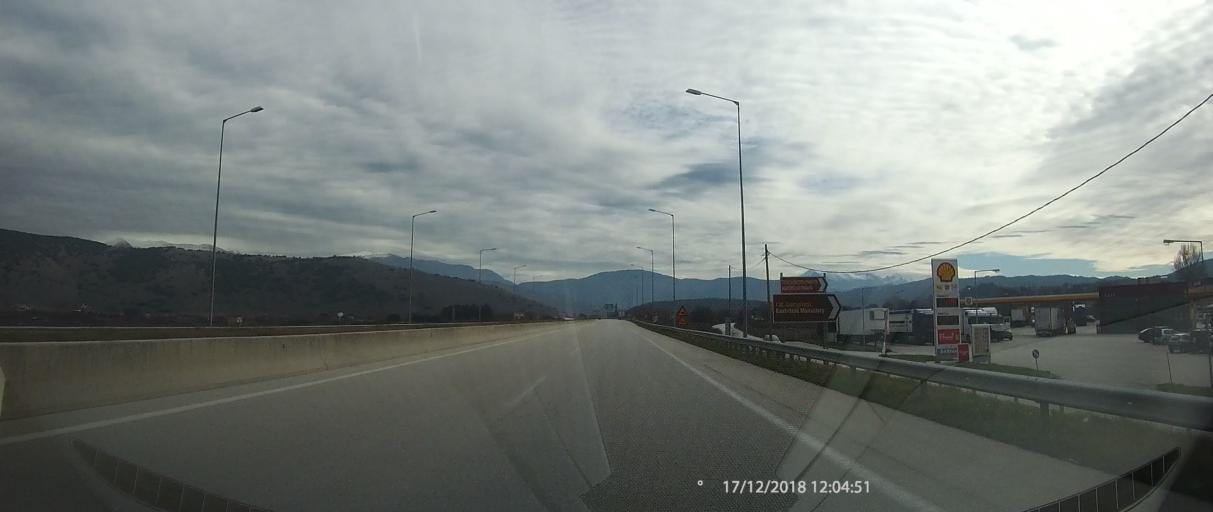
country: GR
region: Epirus
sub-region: Nomos Ioanninon
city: Koutselio
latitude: 39.6017
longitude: 20.8953
